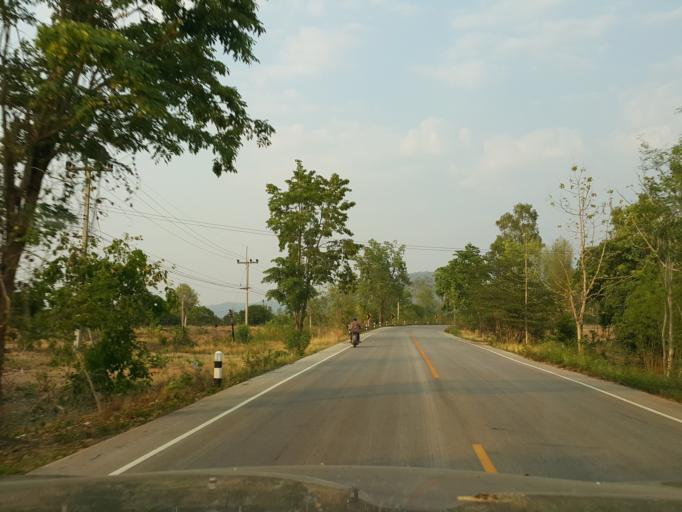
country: TH
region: Lamphun
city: Li
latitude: 17.8189
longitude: 98.9716
